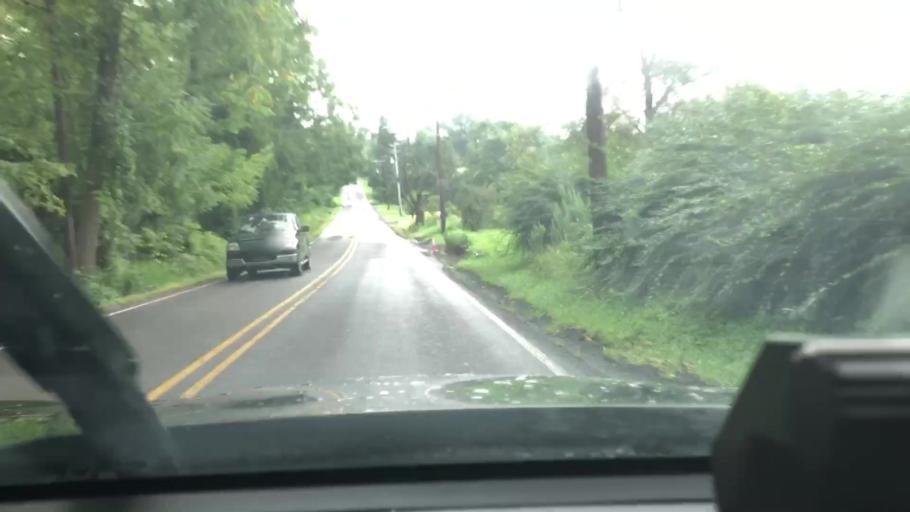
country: US
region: Pennsylvania
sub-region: Lehigh County
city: Coopersburg
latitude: 40.4860
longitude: -75.3944
